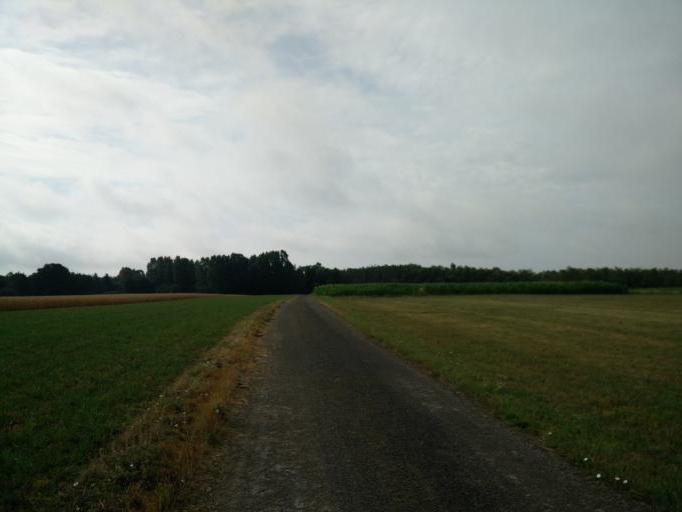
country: LU
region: Luxembourg
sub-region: Canton de Capellen
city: Mamer
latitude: 49.6338
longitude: 6.0410
